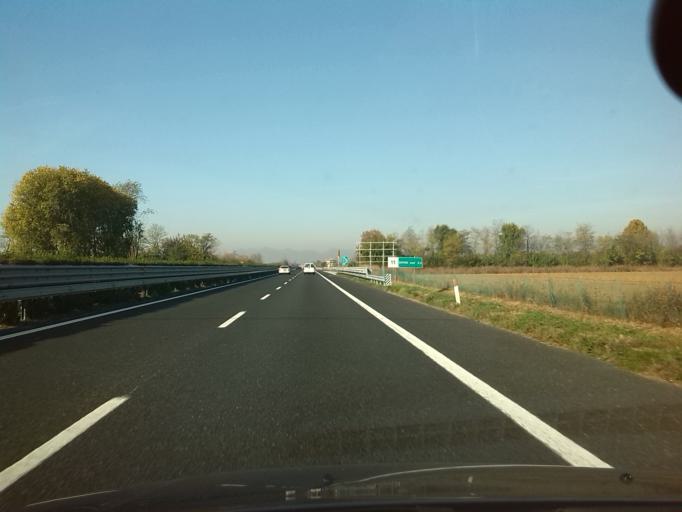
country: IT
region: Friuli Venezia Giulia
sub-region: Provincia di Udine
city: Zugliano-Terenzano-Cargnacco
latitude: 45.9877
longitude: 13.2387
